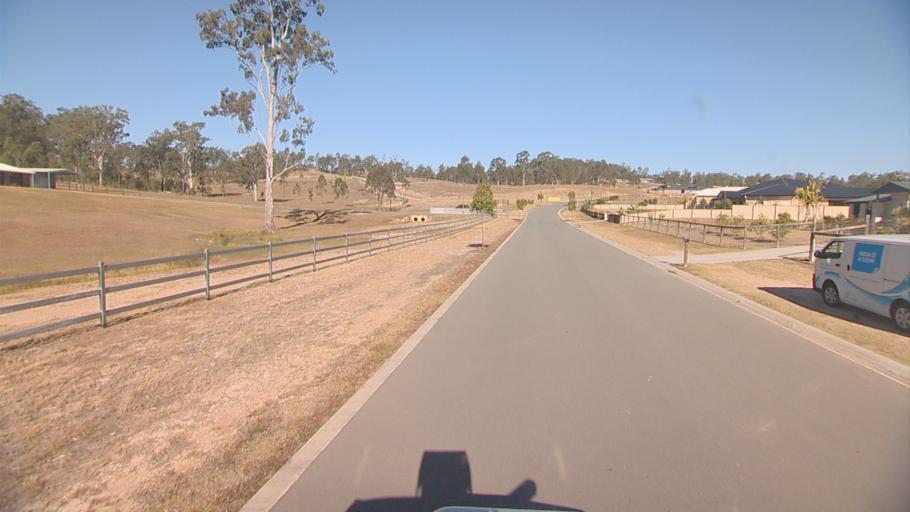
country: AU
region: Queensland
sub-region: Logan
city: Cedar Vale
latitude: -27.8703
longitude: 153.0558
